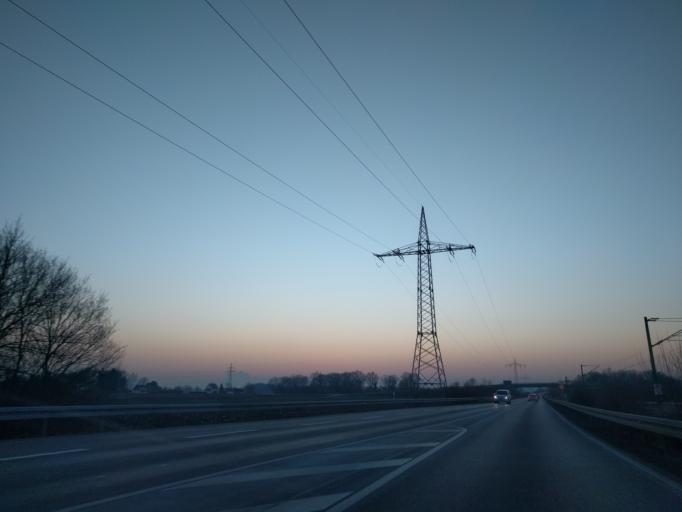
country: DE
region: Bavaria
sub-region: Swabia
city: Asbach-Baumenheim
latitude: 48.6926
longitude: 10.8110
